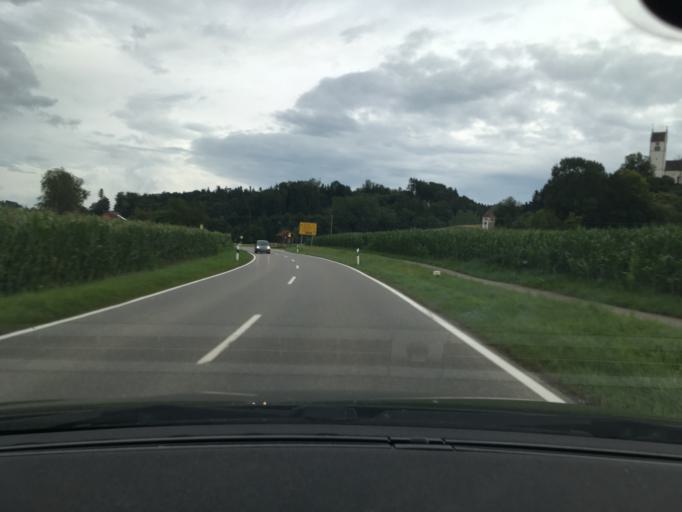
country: DE
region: Baden-Wuerttemberg
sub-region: Tuebingen Region
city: Markdorf
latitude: 47.7743
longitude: 9.4036
